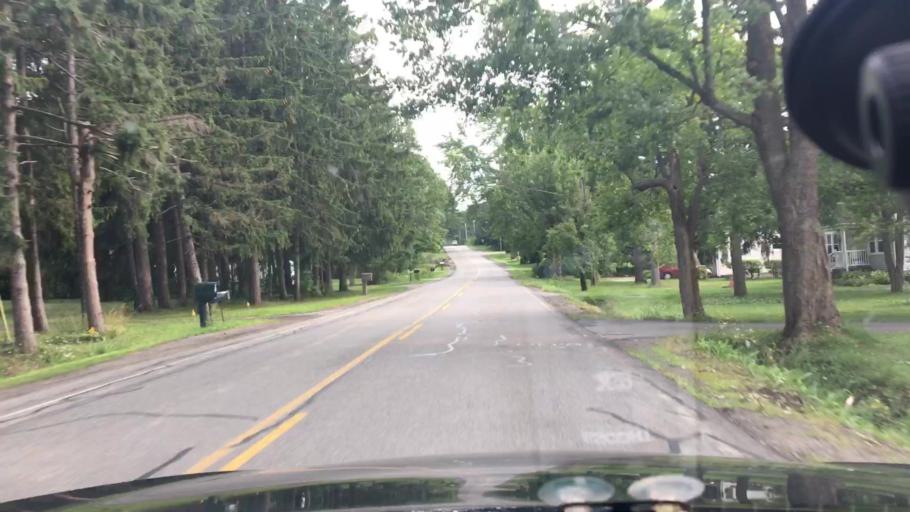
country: US
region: New York
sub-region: Erie County
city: Orchard Park
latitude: 42.7330
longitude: -78.7322
